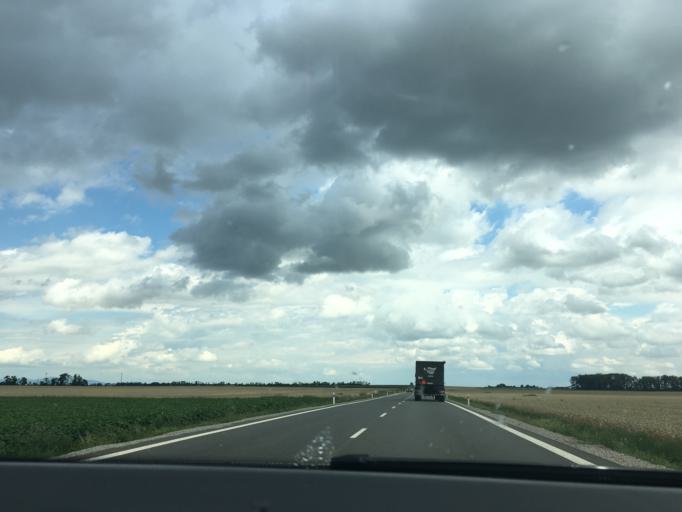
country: SK
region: Kosicky
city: Trebisov
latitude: 48.5551
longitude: 21.6952
